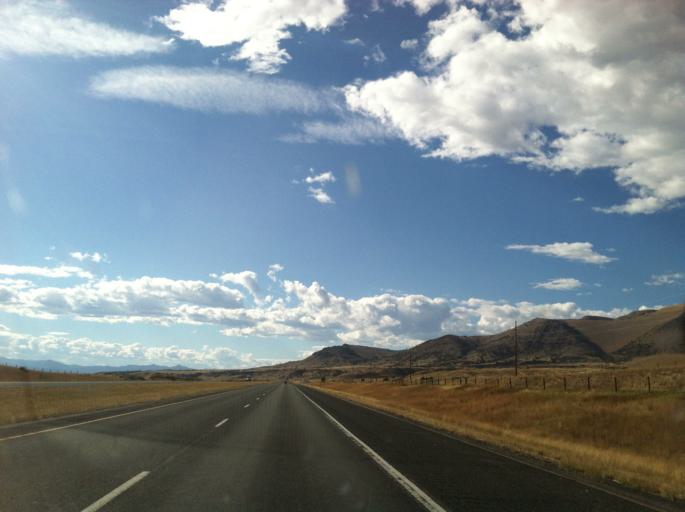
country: US
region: Montana
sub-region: Jefferson County
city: Whitehall
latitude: 45.8753
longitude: -111.9903
